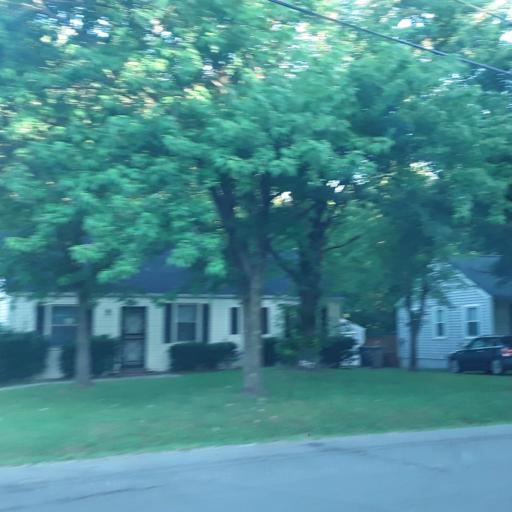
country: US
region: Tennessee
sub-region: Davidson County
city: Oak Hill
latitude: 36.1080
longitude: -86.7347
